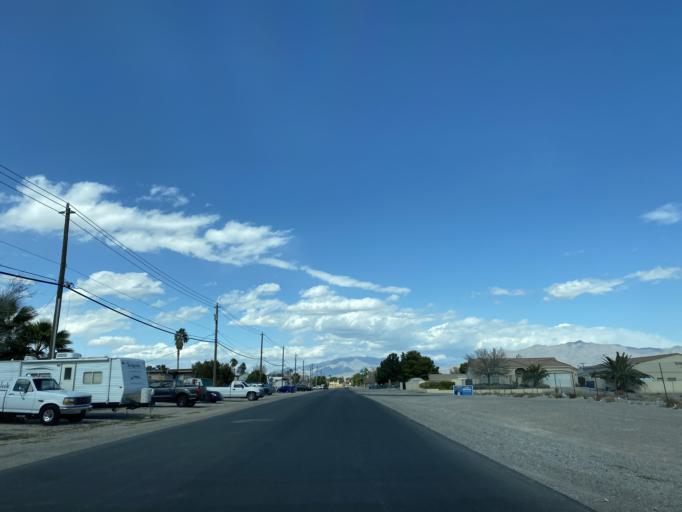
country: US
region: Nevada
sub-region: Clark County
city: Spring Valley
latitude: 36.2489
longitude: -115.2604
